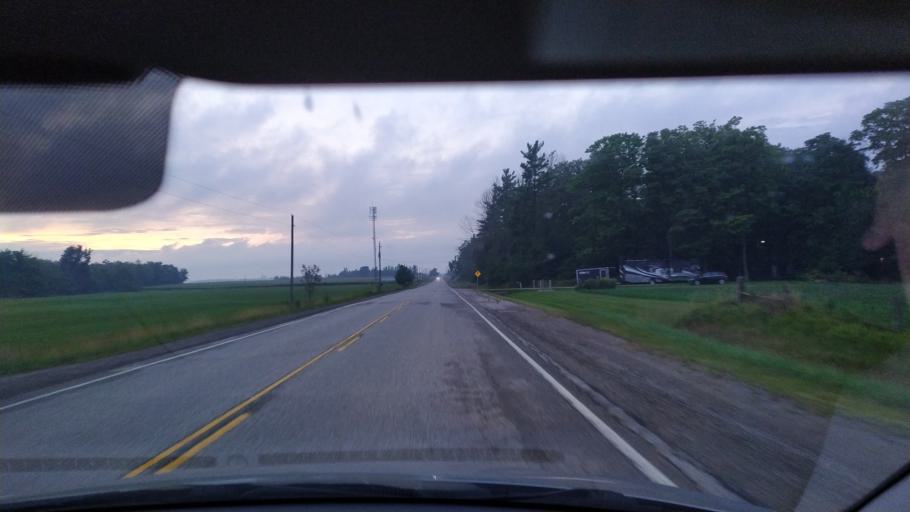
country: CA
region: Ontario
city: Kitchener
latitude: 43.3585
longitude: -80.7047
